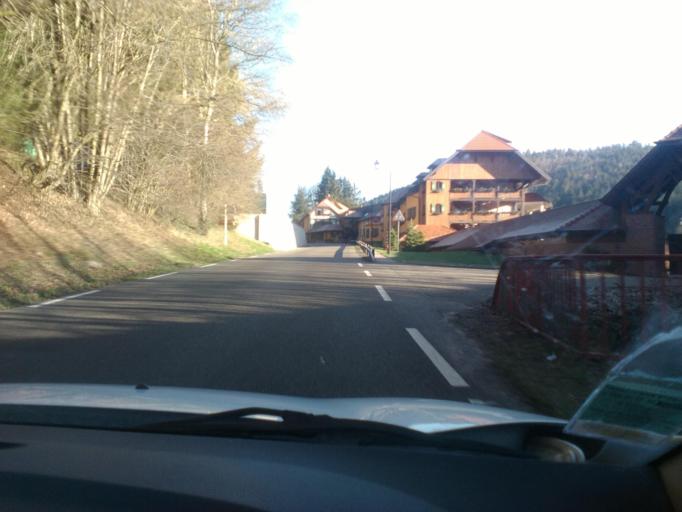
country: FR
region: Alsace
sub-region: Departement du Bas-Rhin
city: Rothau
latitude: 48.4221
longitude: 7.1838
